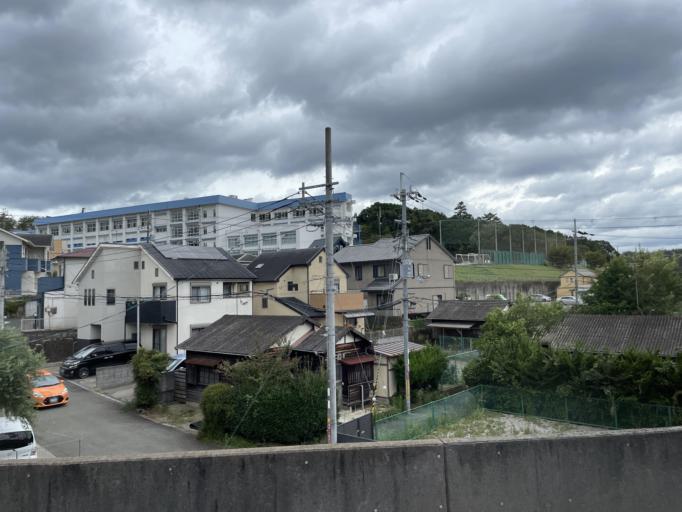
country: JP
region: Osaka
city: Ikeda
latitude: 34.8924
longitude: 135.4117
